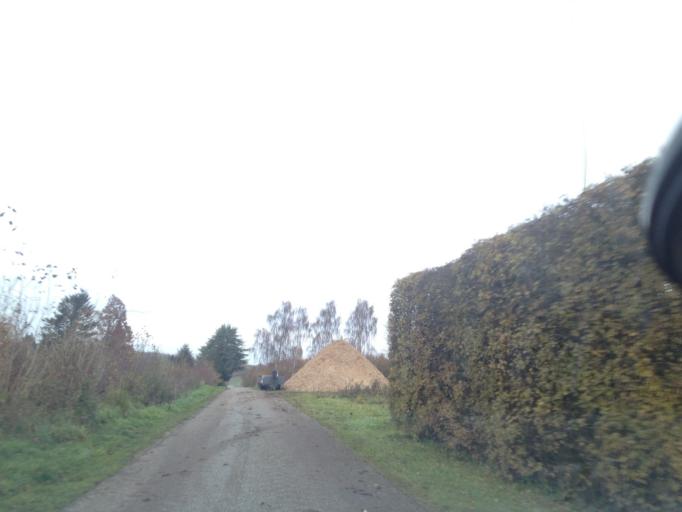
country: DK
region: South Denmark
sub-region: Assens Kommune
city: Vissenbjerg
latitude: 55.4136
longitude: 10.1551
